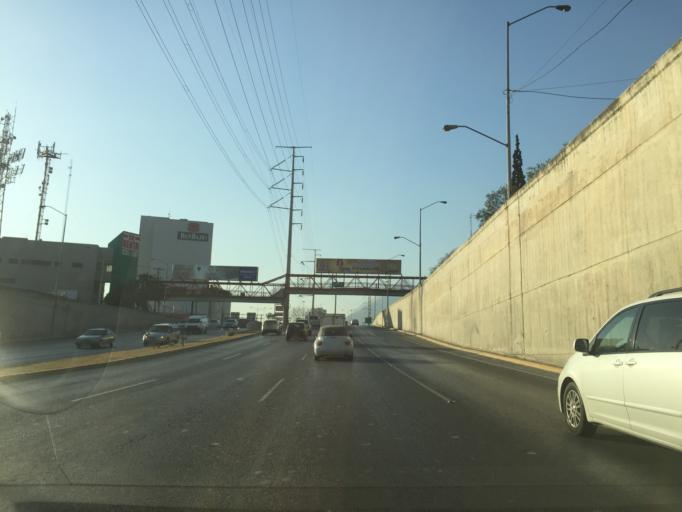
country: MX
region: Nuevo Leon
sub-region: Monterrey
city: Monterrey
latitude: 25.6520
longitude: -100.3342
